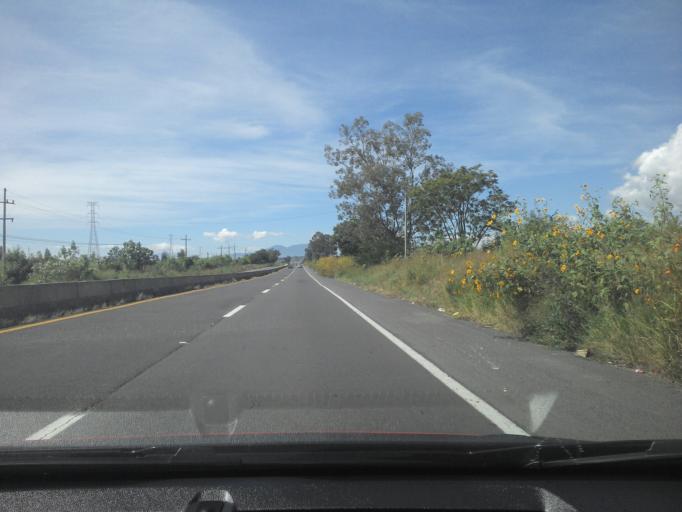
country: MX
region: Jalisco
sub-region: Tala
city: Los Ruisenores
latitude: 20.7109
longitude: -103.6630
